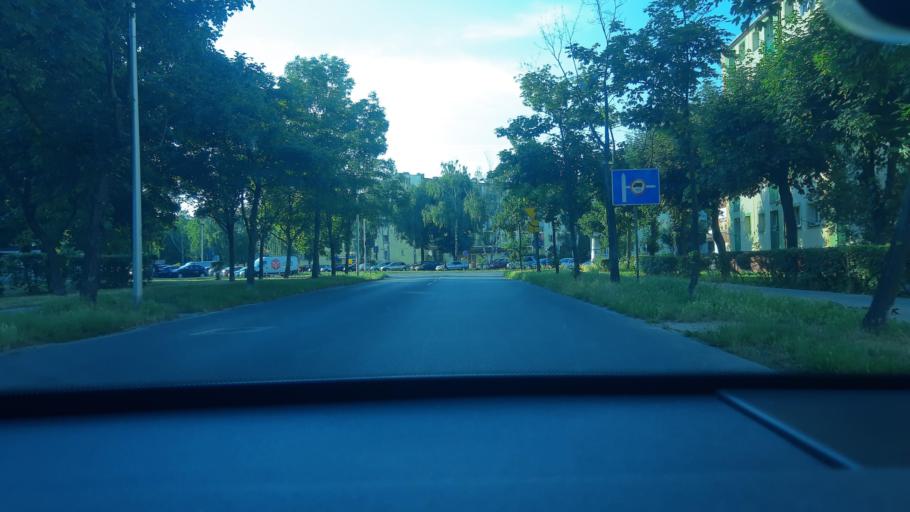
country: PL
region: Lodz Voivodeship
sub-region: Powiat sieradzki
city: Sieradz
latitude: 51.5889
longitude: 18.7315
